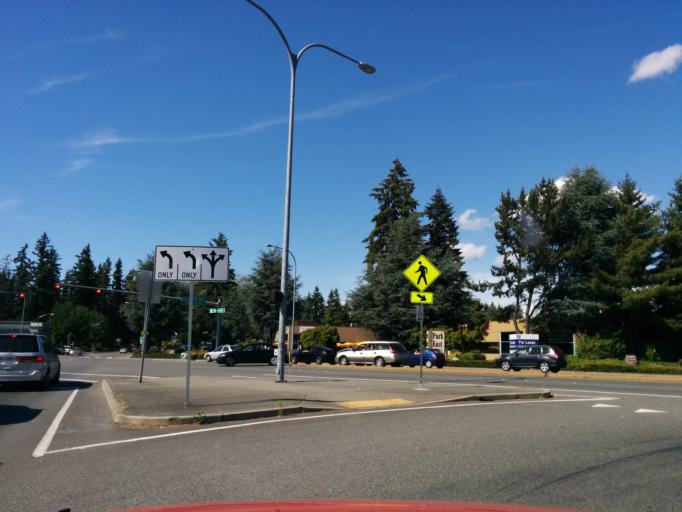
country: US
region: Washington
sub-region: King County
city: Redmond
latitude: 47.6652
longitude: -122.0998
